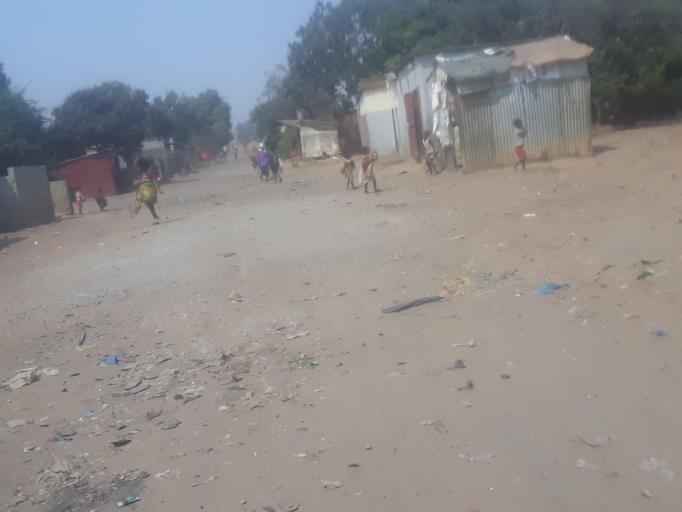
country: ZM
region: Lusaka
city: Lusaka
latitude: -15.3534
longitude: 28.2870
